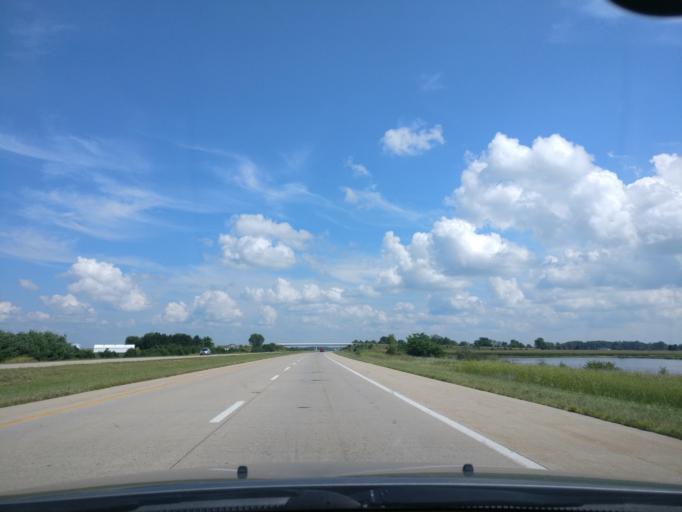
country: US
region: Ohio
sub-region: Greene County
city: Wilberforce
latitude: 39.6863
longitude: -83.8524
